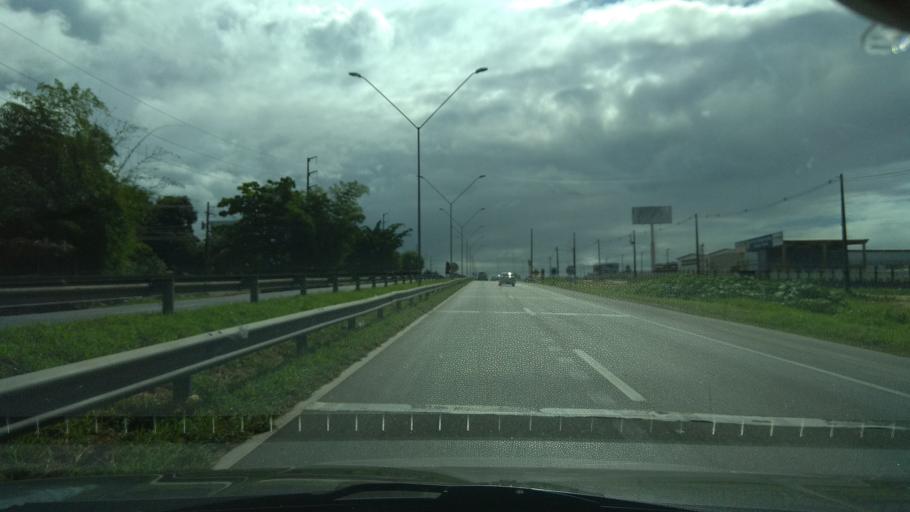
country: BR
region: Bahia
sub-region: Conceicao Do Jacuipe
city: Conceicao do Jacuipe
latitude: -12.3219
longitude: -38.8699
